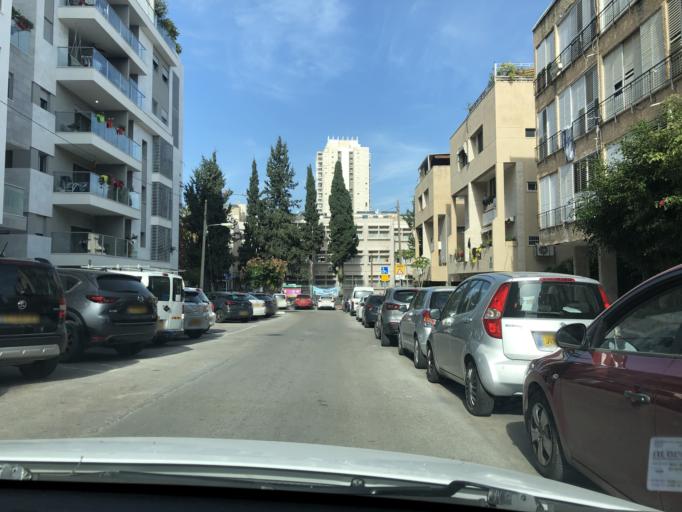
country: IL
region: Tel Aviv
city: Bene Beraq
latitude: 32.0684
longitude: 34.8279
